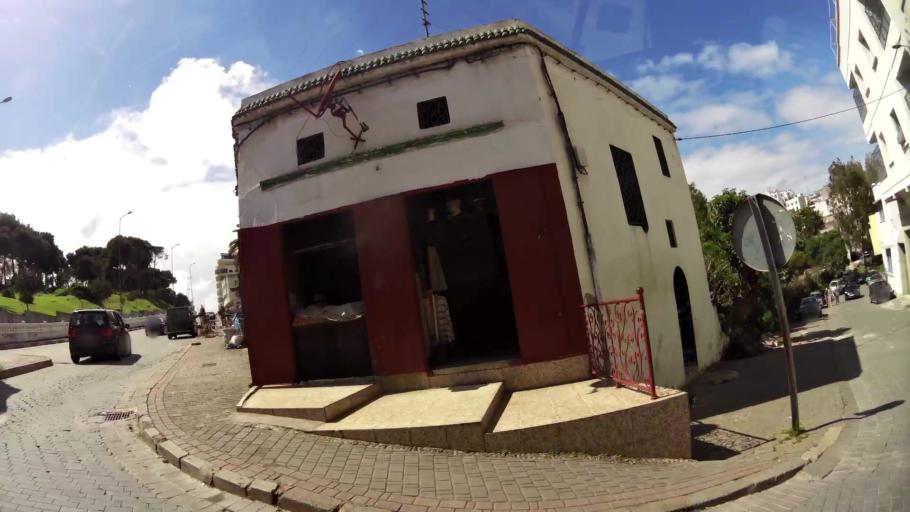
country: MA
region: Tanger-Tetouan
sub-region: Tanger-Assilah
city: Tangier
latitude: 35.7844
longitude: -5.8166
